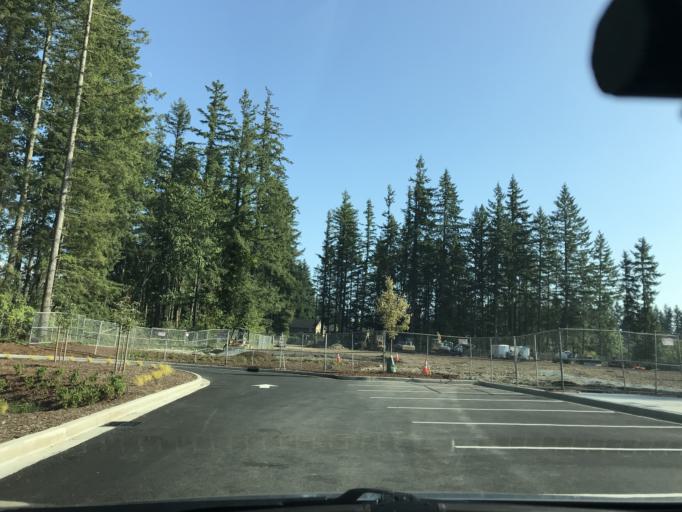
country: US
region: Washington
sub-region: King County
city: Ravensdale
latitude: 47.3559
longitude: -122.0211
